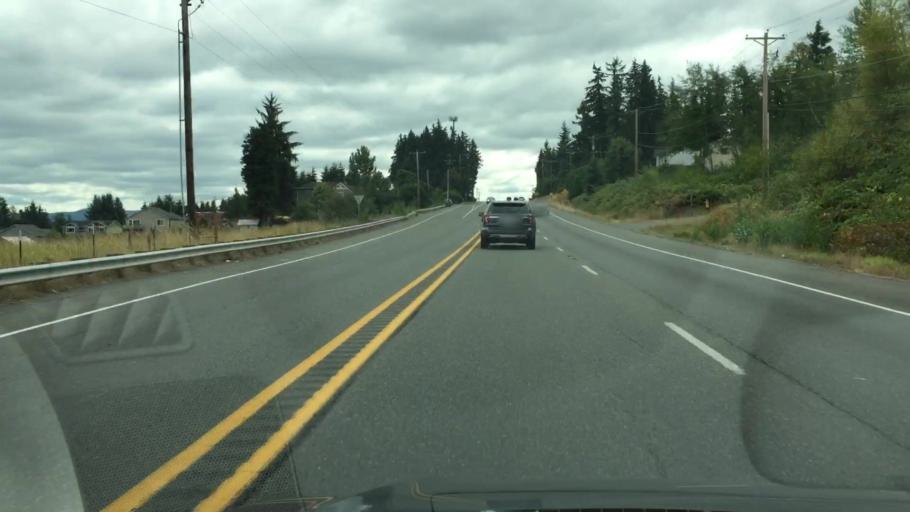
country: US
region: Washington
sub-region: Pierce County
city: Graham
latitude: 47.0323
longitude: -122.2959
